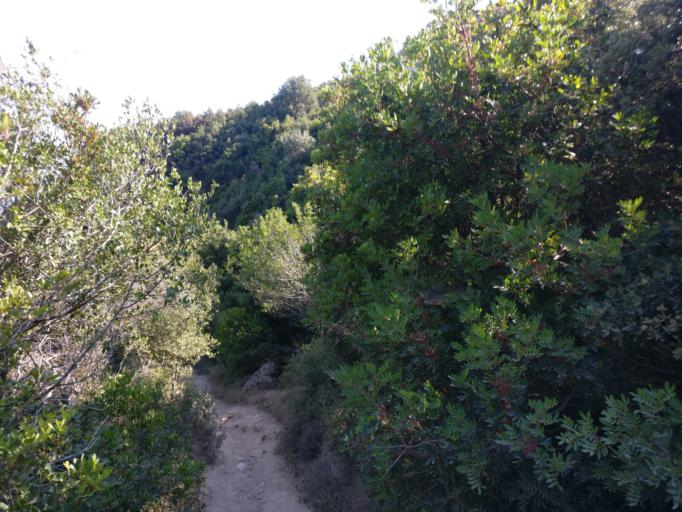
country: GR
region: Ionian Islands
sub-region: Nomos Kerkyras
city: Agios Georgis
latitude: 39.7174
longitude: 19.6583
